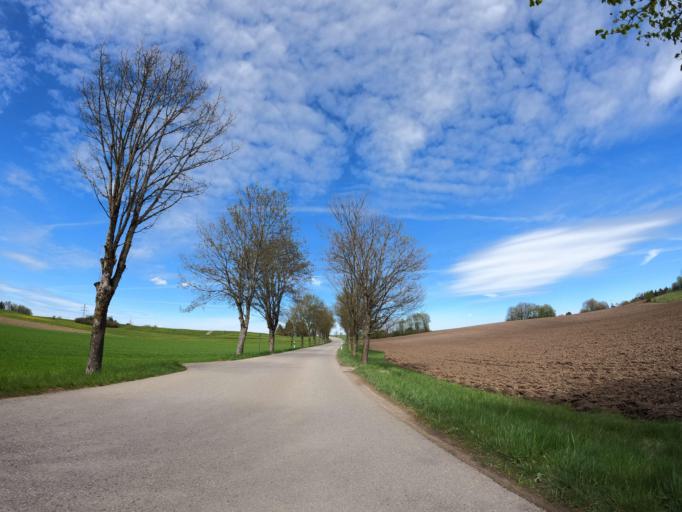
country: DE
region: Bavaria
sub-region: Upper Bavaria
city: Strasslach-Dingharting
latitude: 47.9738
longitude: 11.5170
